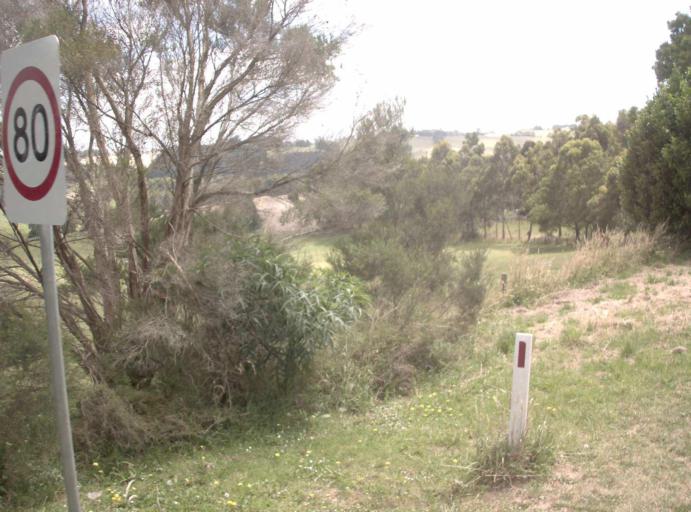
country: AU
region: Victoria
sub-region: Baw Baw
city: Warragul
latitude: -38.4086
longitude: 145.8128
